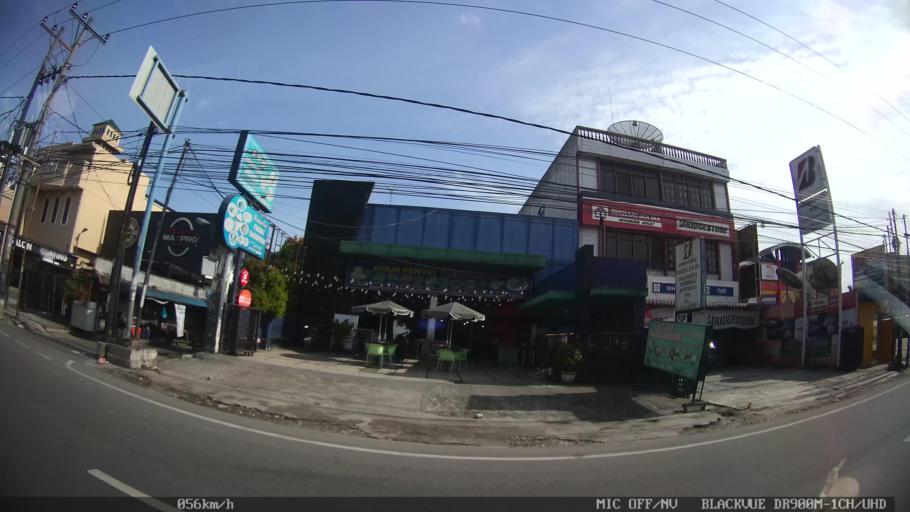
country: ID
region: North Sumatra
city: Medan
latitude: 3.5905
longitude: 98.6515
